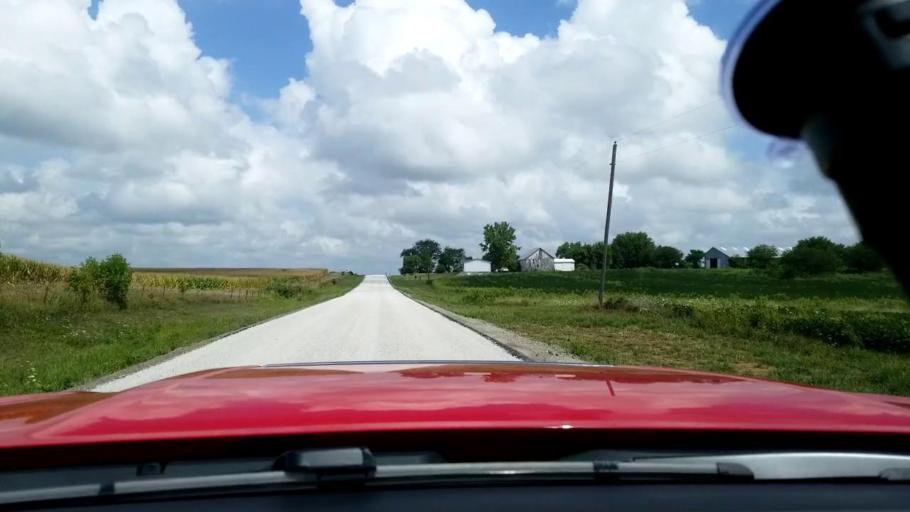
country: US
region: Iowa
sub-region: Decatur County
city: Lamoni
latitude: 40.6358
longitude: -94.0531
